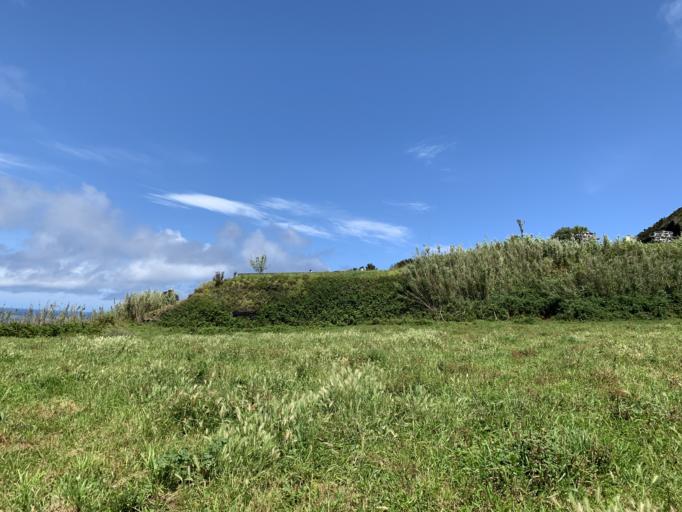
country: PT
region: Azores
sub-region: Ponta Delgada
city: Arrifes
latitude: 37.8572
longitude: -25.8505
